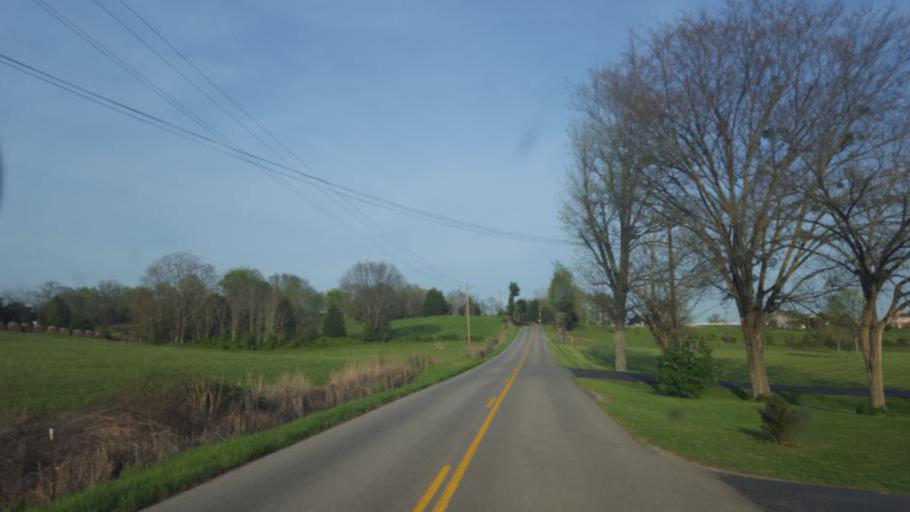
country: US
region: Kentucky
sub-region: Barren County
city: Glasgow
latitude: 36.9482
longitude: -86.0087
